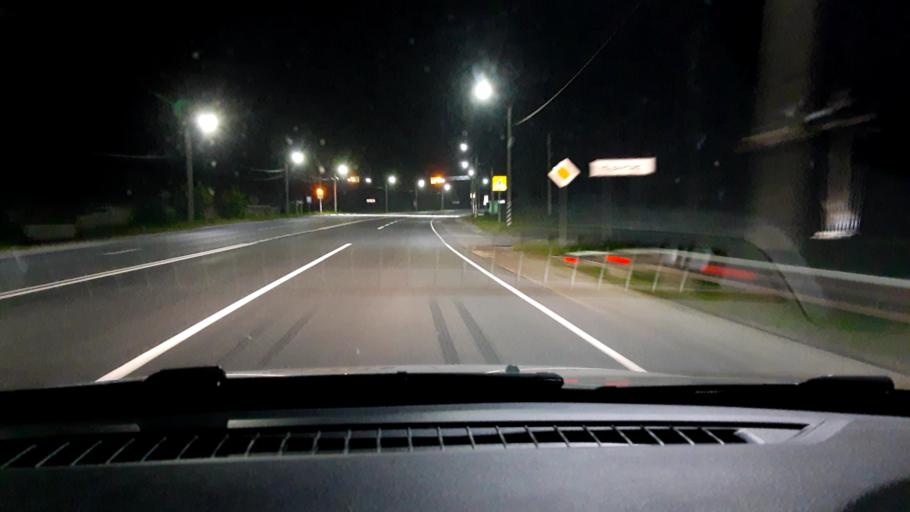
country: RU
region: Nizjnij Novgorod
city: Sitniki
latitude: 56.5056
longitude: 44.0238
